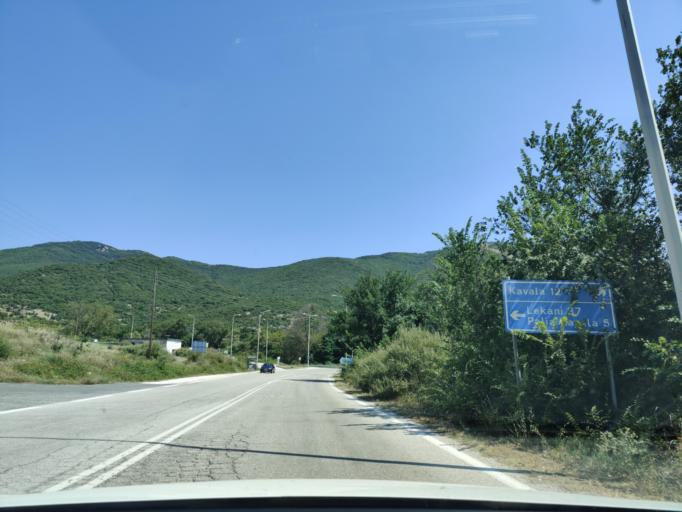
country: GR
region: East Macedonia and Thrace
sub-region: Nomos Kavalas
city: Zygos
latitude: 40.9971
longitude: 24.3823
